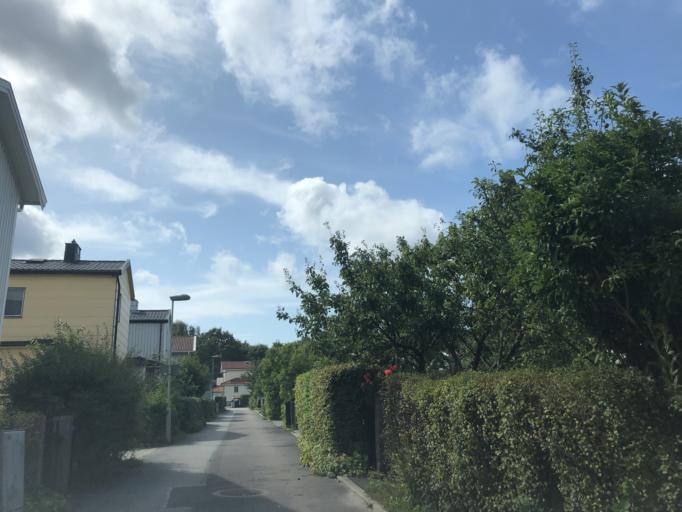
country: SE
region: Vaestra Goetaland
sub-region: Goteborg
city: Majorna
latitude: 57.7049
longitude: 11.8970
